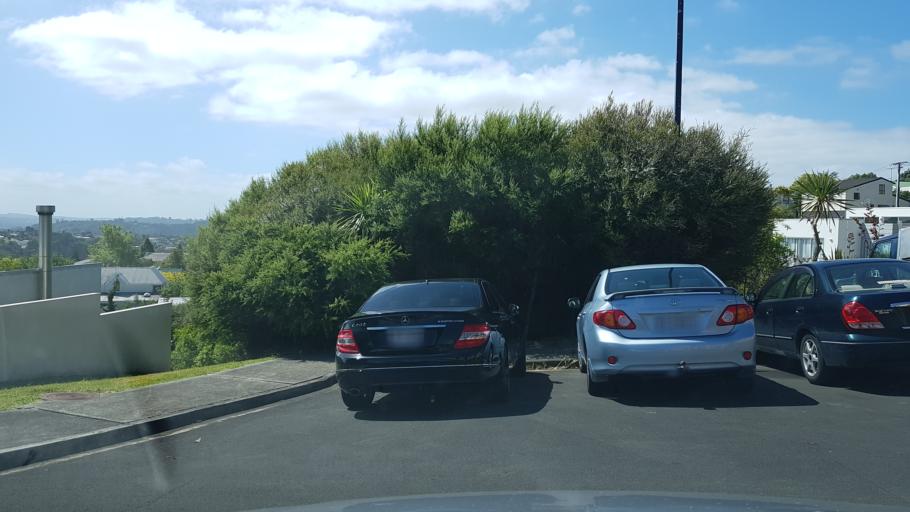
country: NZ
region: Auckland
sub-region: Auckland
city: North Shore
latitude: -36.8063
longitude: 174.7035
